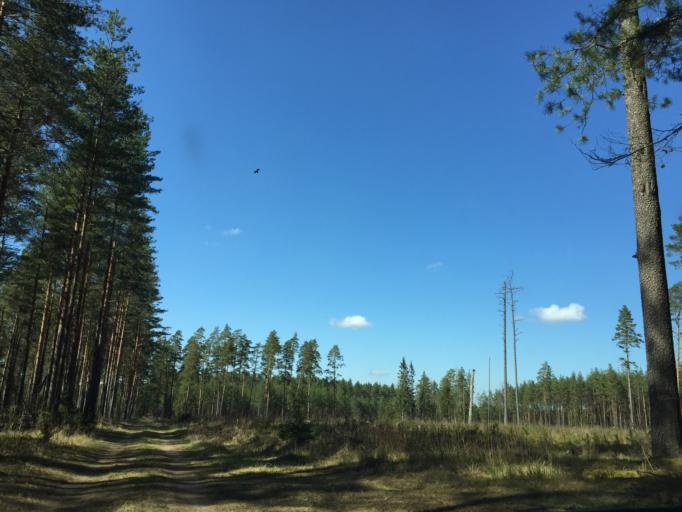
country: LV
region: Strenci
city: Strenci
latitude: 57.5960
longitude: 25.7086
